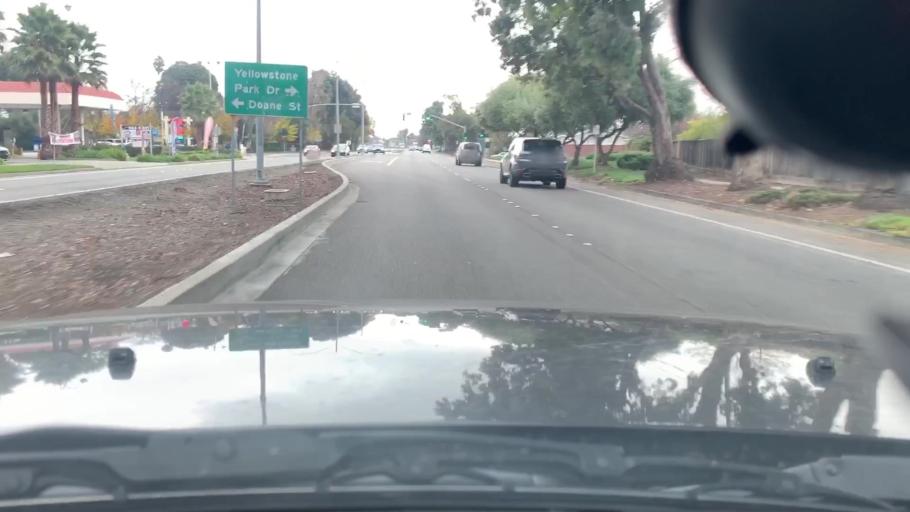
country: US
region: California
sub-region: Alameda County
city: Fremont
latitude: 37.5138
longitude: -121.9658
